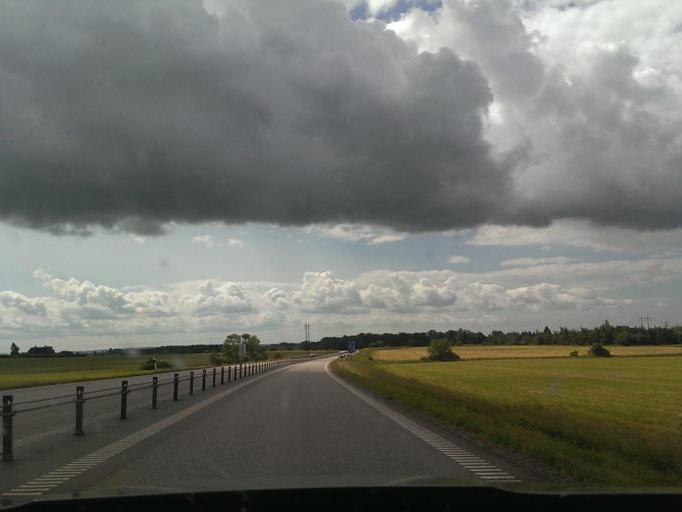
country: SE
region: Skane
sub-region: Eslovs Kommun
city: Eslov
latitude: 55.8205
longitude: 13.3358
